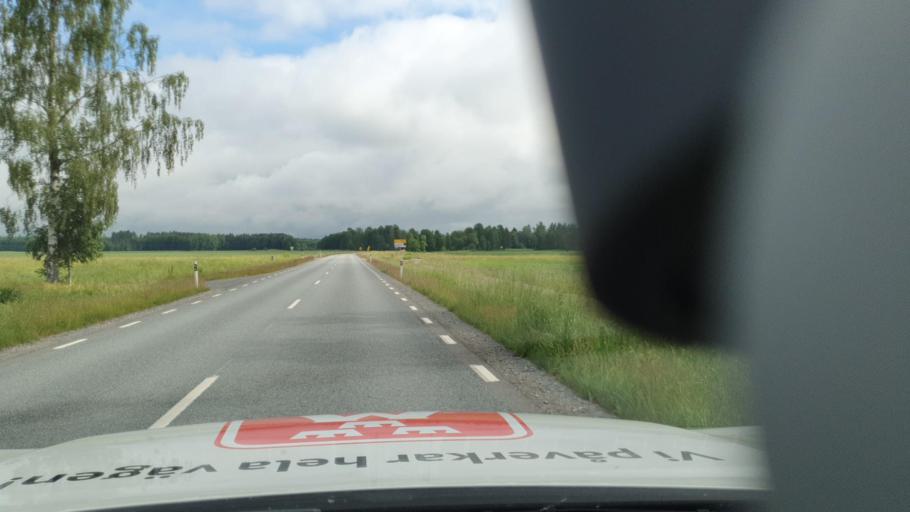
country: SE
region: Vaestra Goetaland
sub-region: Gullspangs Kommun
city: Anderstorp
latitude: 59.0679
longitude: 14.2904
